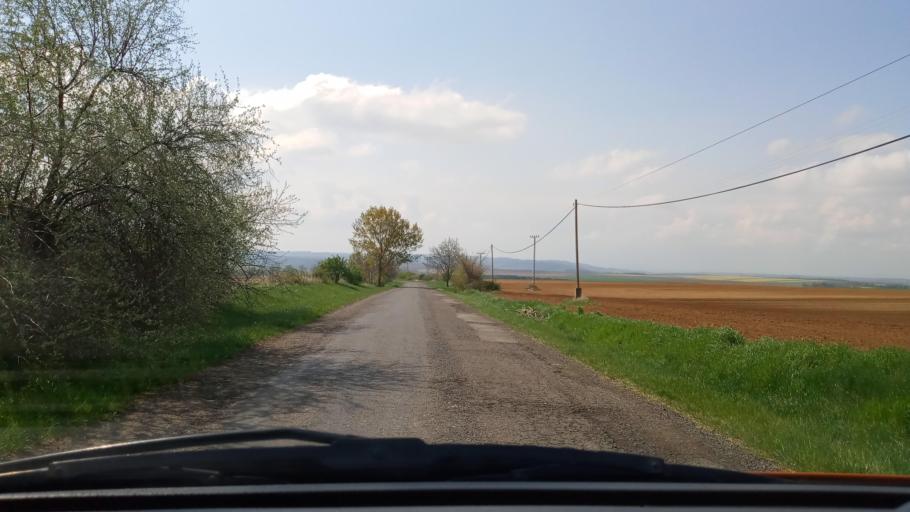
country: HU
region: Baranya
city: Pecsvarad
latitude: 46.1054
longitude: 18.4962
